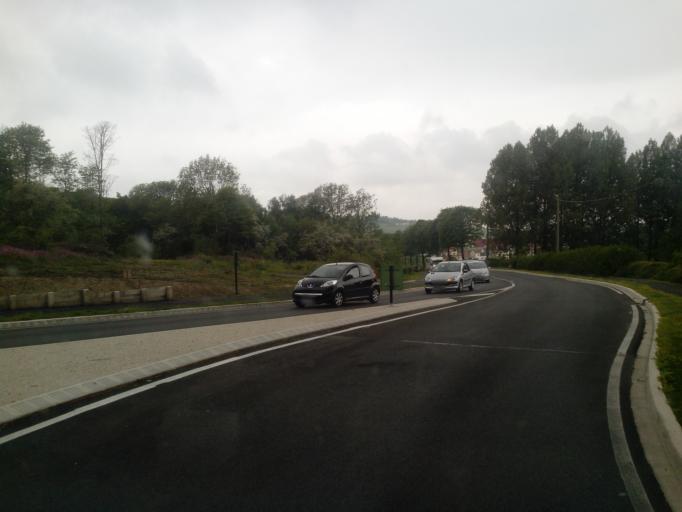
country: FR
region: Nord-Pas-de-Calais
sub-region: Departement du Pas-de-Calais
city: Condette
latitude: 50.6660
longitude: 1.6401
